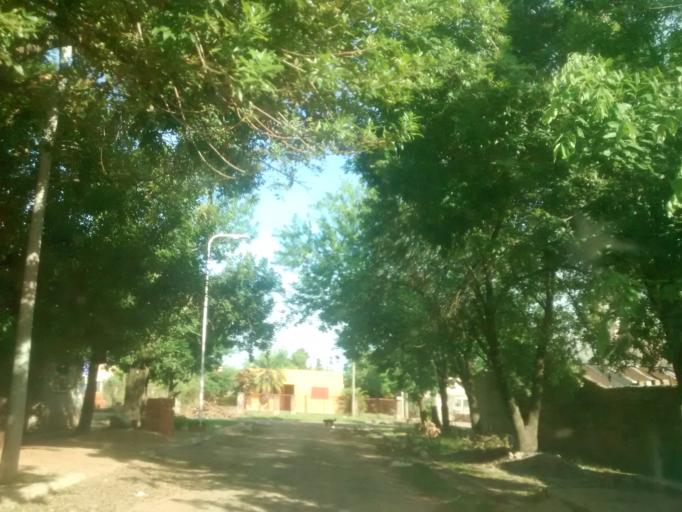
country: AR
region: Chaco
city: Puerto Tirol
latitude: -27.3752
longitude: -59.0924
